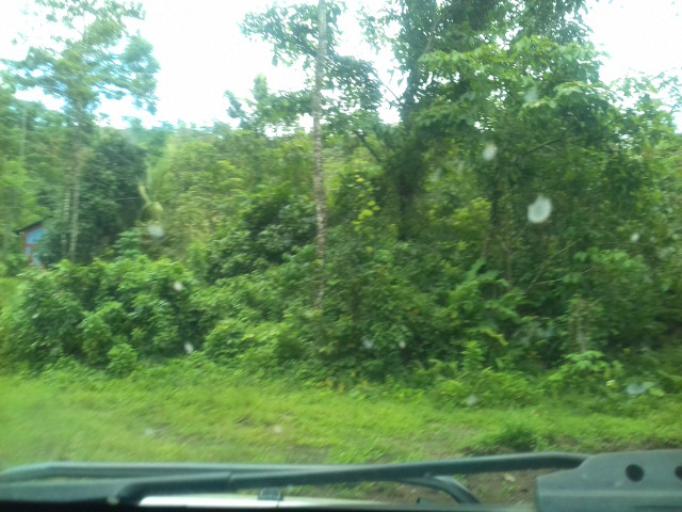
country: NI
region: Matagalpa
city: Rio Blanco
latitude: 13.0324
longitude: -85.2342
